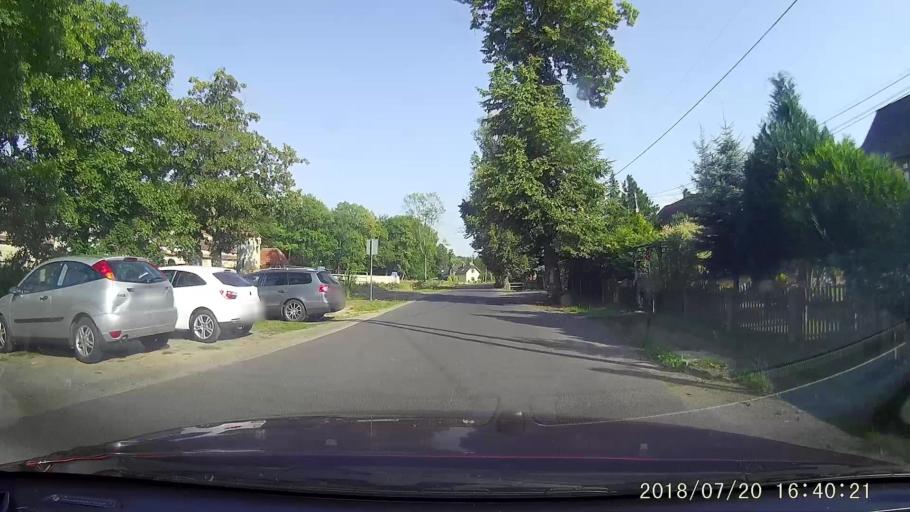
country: PL
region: Lower Silesian Voivodeship
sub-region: Powiat lubanski
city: Siekierczyn
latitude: 51.0861
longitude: 15.1461
